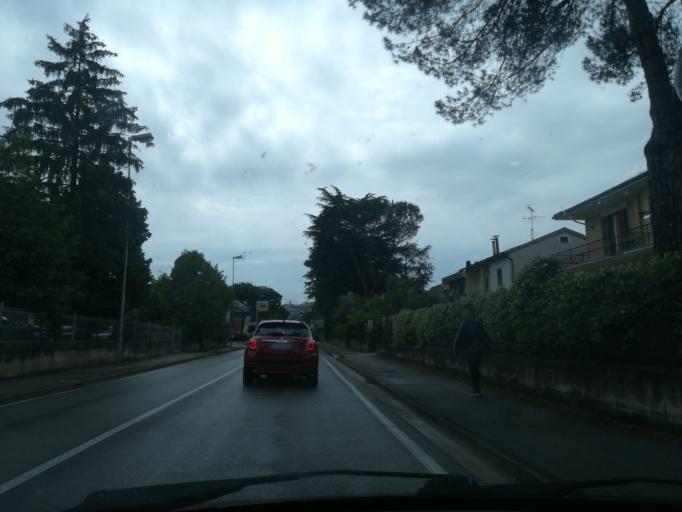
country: IT
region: The Marches
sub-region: Provincia di Macerata
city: Zona Industriale
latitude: 43.2639
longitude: 13.4913
